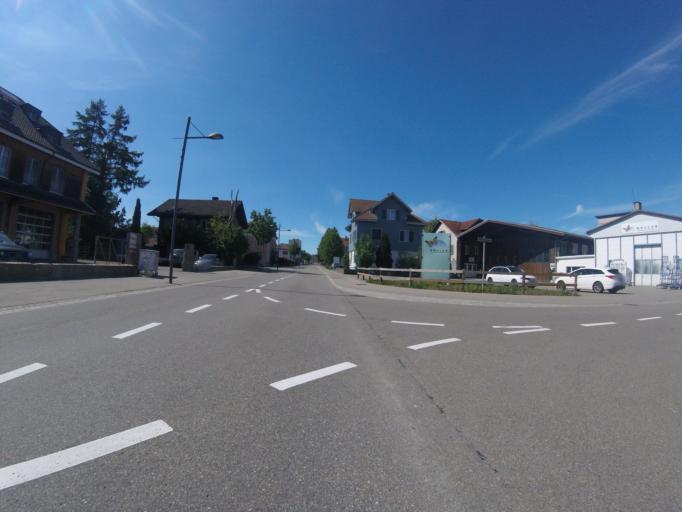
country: CH
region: Saint Gallen
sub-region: Wahlkreis Toggenburg
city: Lutisburg
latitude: 47.4090
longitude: 9.0710
